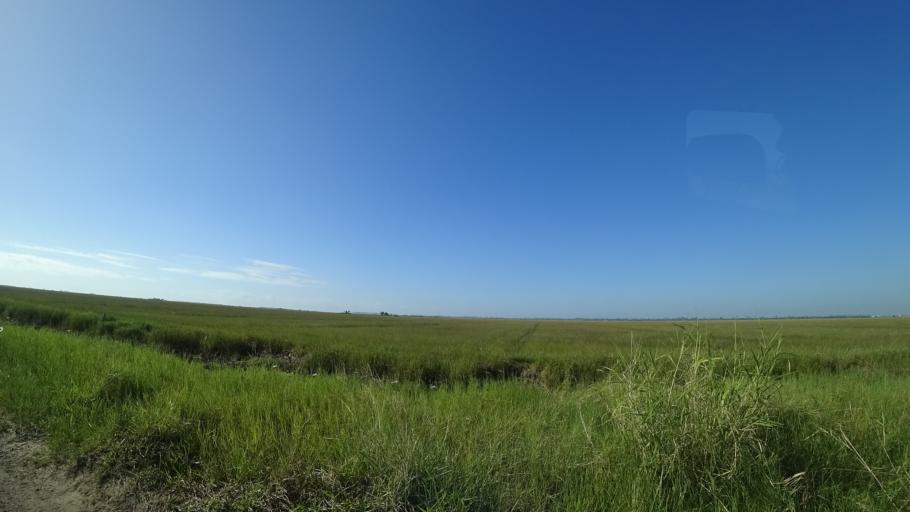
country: MZ
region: Sofala
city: Beira
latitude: -19.7576
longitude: 34.9201
